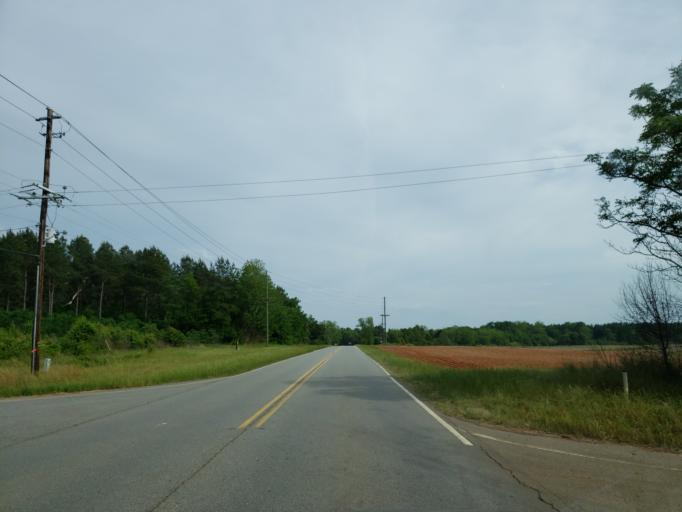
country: US
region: Georgia
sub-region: Dooly County
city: Vienna
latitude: 32.1901
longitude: -83.8980
